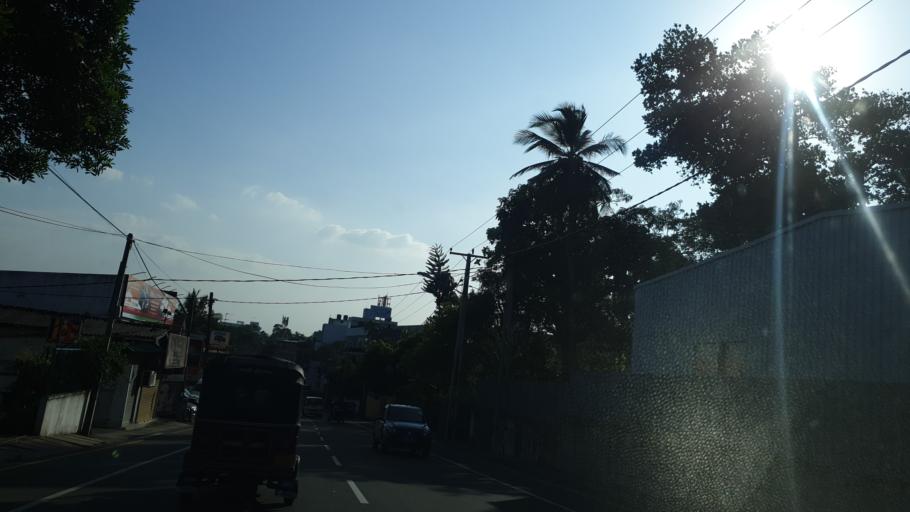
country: LK
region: Western
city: Sri Jayewardenepura Kotte
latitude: 6.8713
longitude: 79.8987
